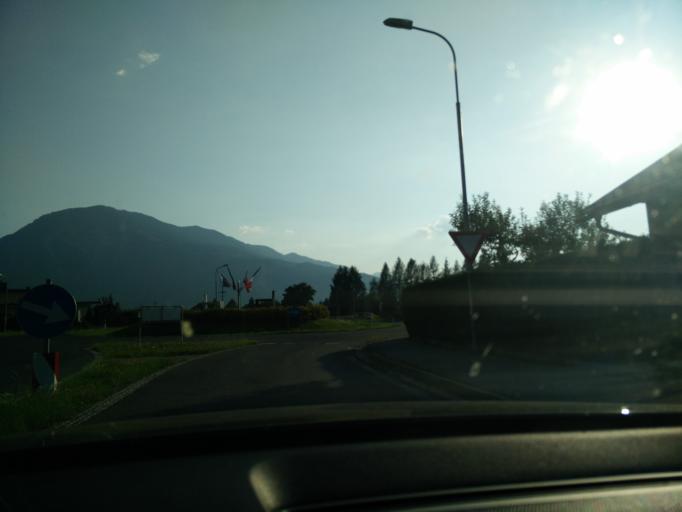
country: AT
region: Carinthia
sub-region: Politischer Bezirk Klagenfurt Land
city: Ferlach
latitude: 46.5382
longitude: 14.3122
